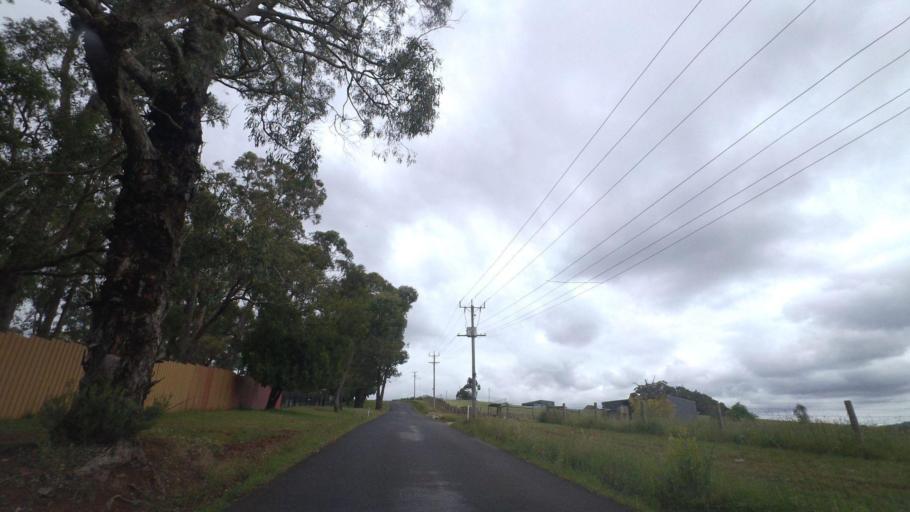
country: AU
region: Victoria
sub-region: Yarra Ranges
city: Mount Evelyn
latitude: -37.7869
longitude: 145.4197
